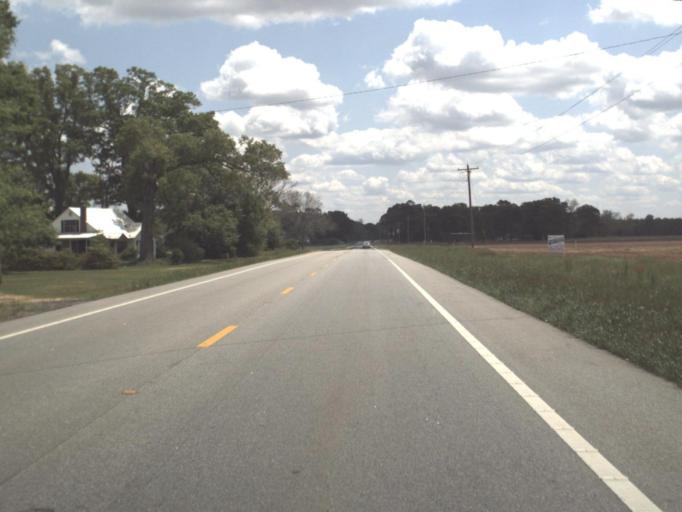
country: US
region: Alabama
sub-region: Escambia County
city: Atmore
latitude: 30.9722
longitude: -87.4880
